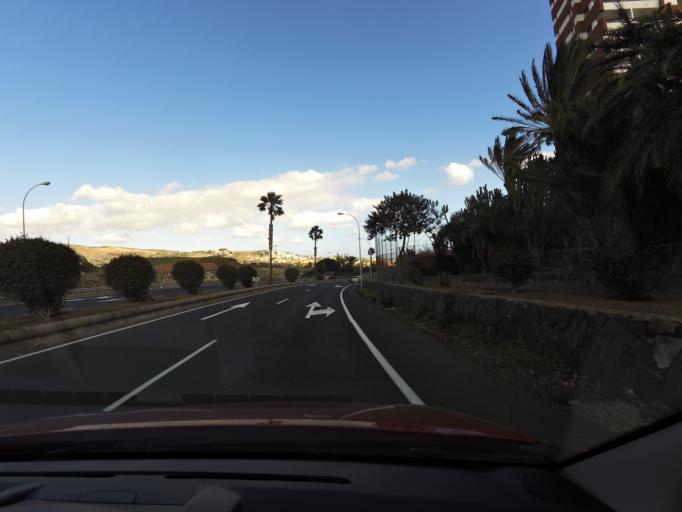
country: ES
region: Canary Islands
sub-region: Provincia de Las Palmas
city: Playa del Ingles
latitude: 27.7656
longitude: -15.5608
